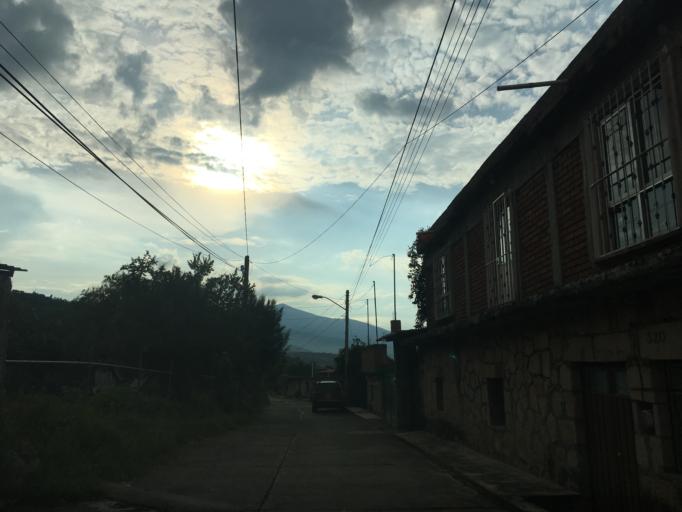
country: MX
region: Michoacan
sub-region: Morelia
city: La Mintzita (Piedra Dura)
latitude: 19.6415
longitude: -101.2635
